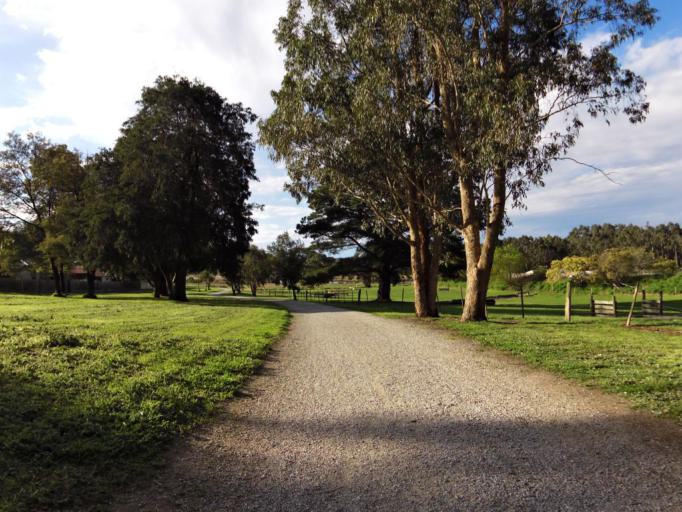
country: AU
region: Victoria
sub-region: Whitehorse
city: Vermont South
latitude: -37.8754
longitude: 145.1890
